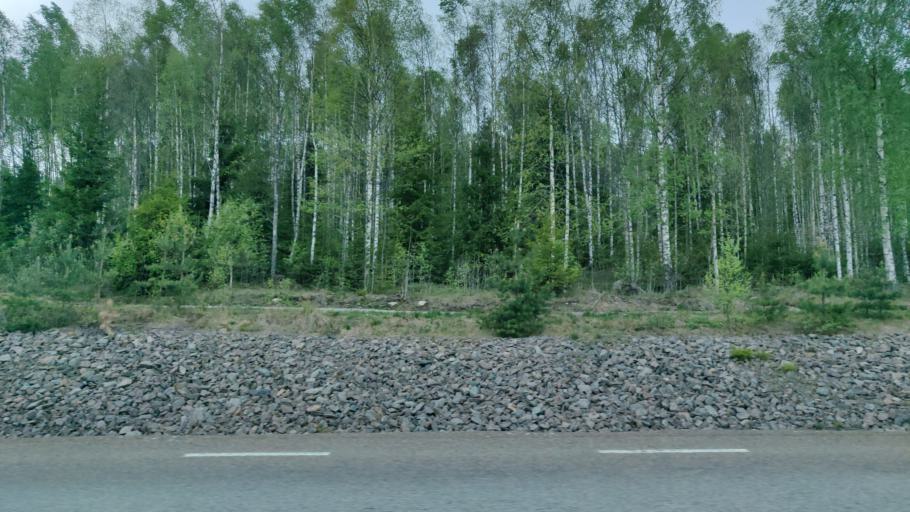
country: SE
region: Vaermland
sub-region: Forshaga Kommun
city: Deje
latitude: 59.6882
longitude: 13.4407
